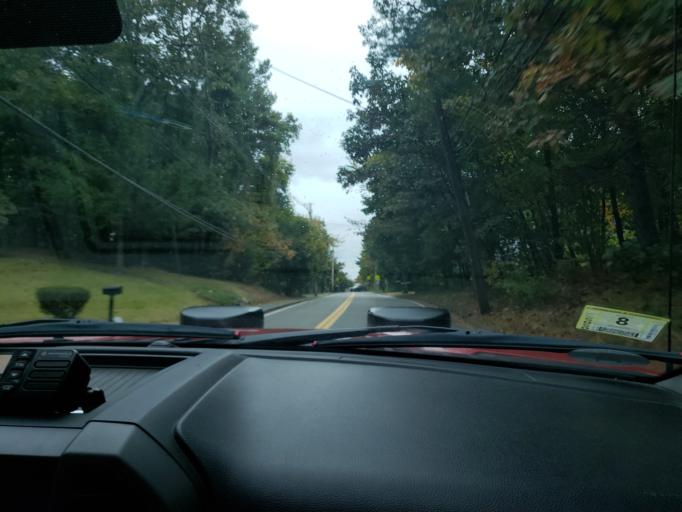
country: US
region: Massachusetts
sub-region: Middlesex County
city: Natick
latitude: 42.2705
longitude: -71.3558
